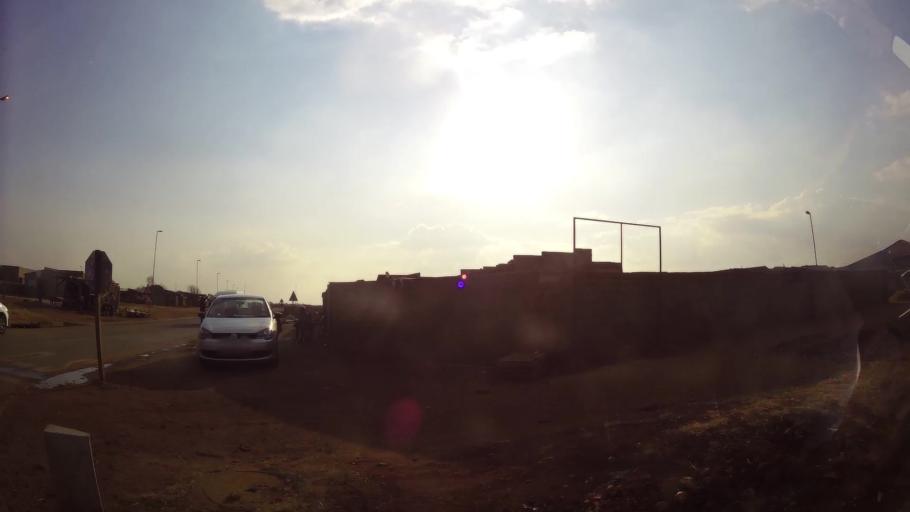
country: ZA
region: Gauteng
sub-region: Ekurhuleni Metropolitan Municipality
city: Germiston
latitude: -26.3701
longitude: 28.1975
